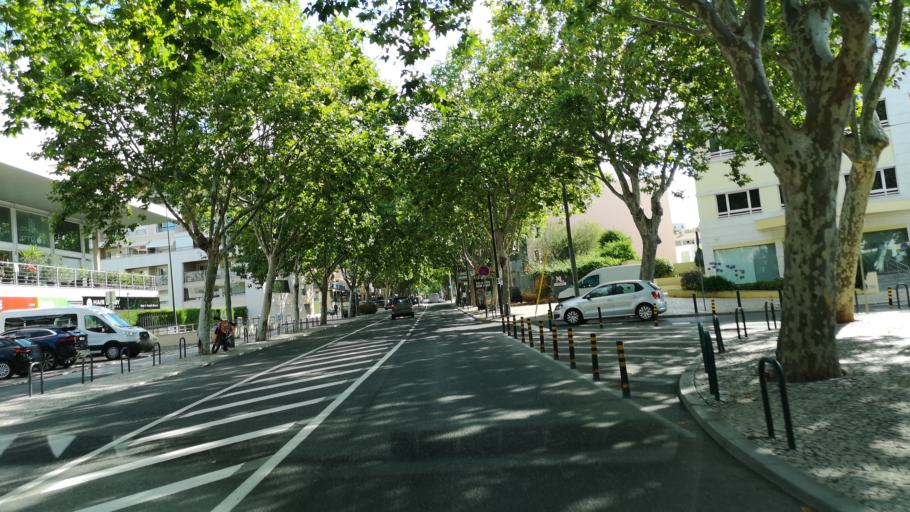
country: PT
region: Lisbon
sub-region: Cascais
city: Cascais
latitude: 38.6980
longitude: -9.4288
